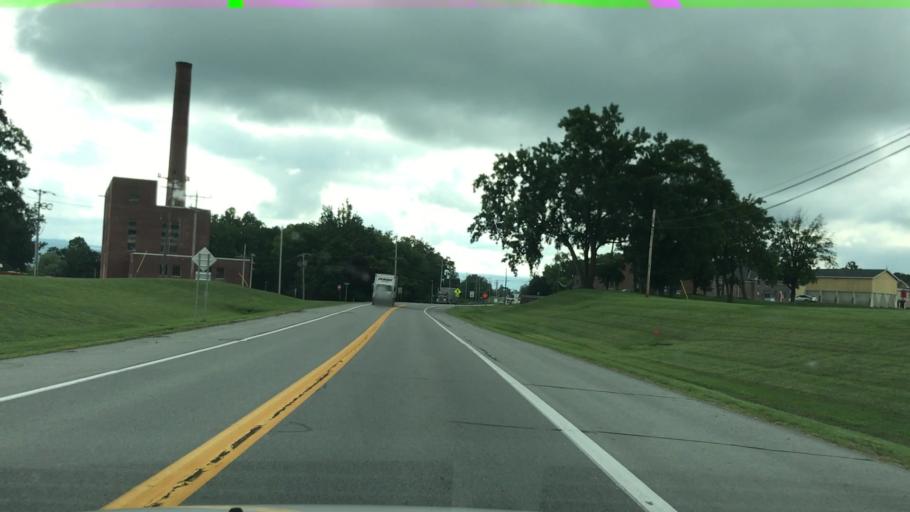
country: US
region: New York
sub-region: Livingston County
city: Mount Morris
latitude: 42.6849
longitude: -77.8320
